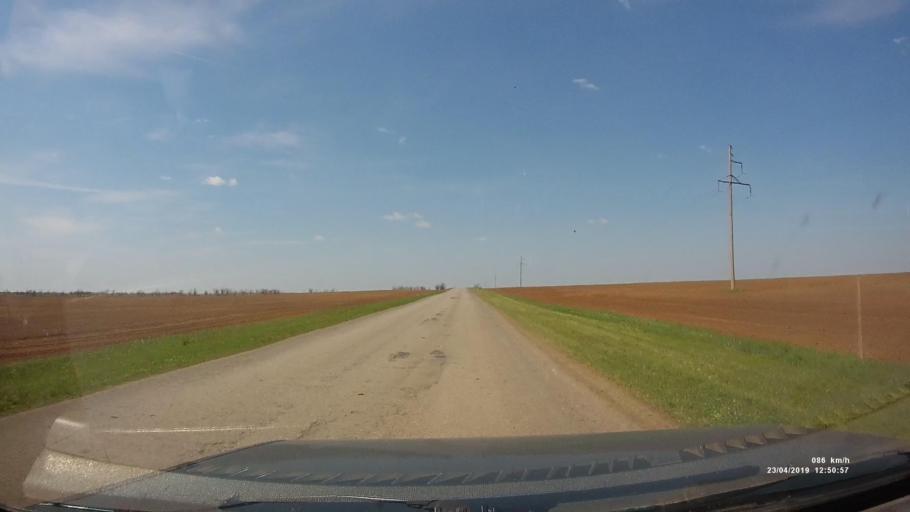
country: RU
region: Kalmykiya
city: Yashalta
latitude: 46.5503
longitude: 42.6291
